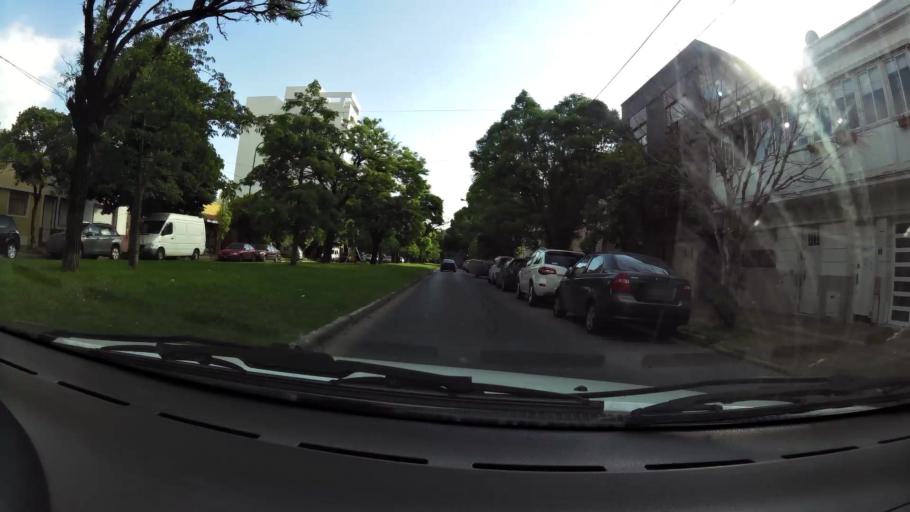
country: AR
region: Buenos Aires
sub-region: Partido de La Plata
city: La Plata
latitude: -34.9030
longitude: -57.9592
